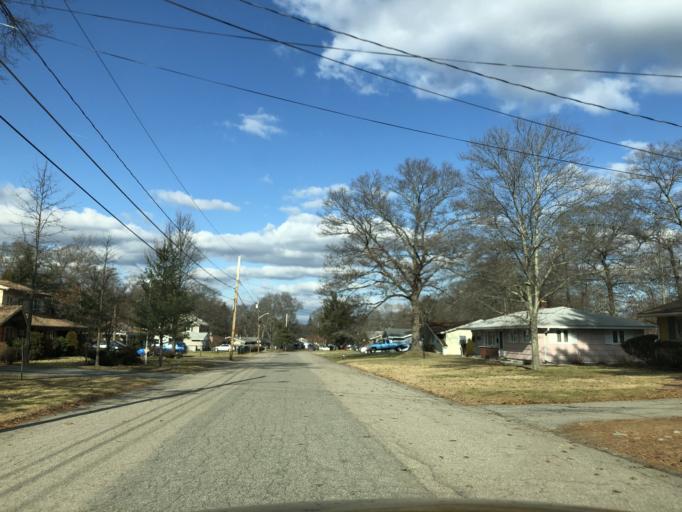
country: US
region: Massachusetts
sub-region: Plymouth County
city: Brockton
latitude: 42.1109
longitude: -71.0049
